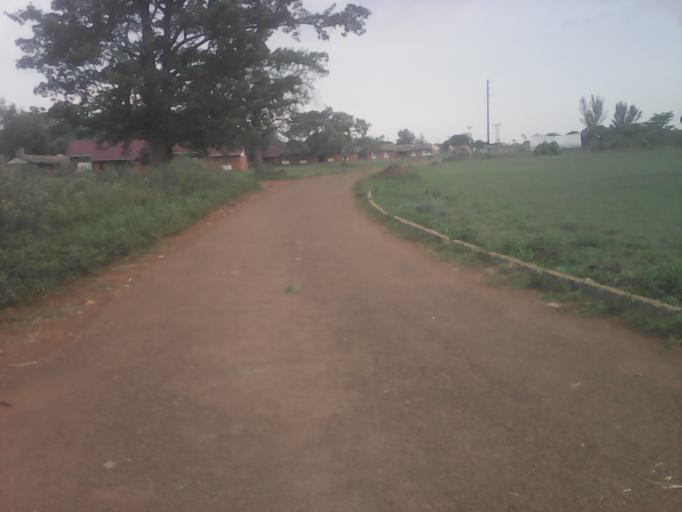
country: UG
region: Eastern Region
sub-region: Busia District
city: Busia
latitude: 0.5473
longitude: 34.0243
